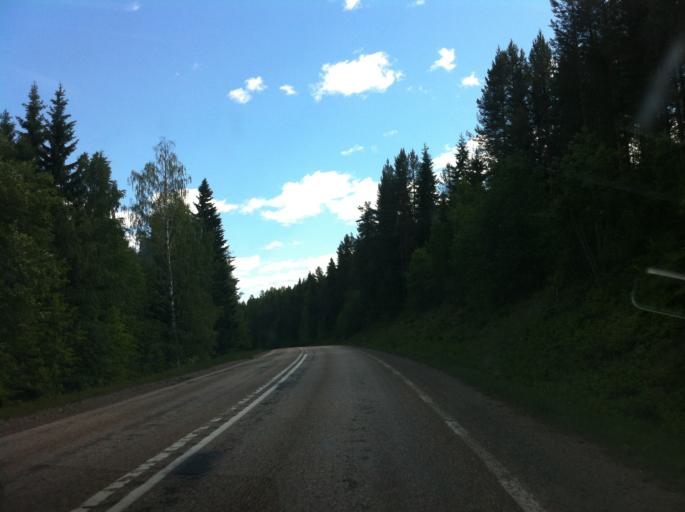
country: SE
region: Gaevleborg
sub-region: Ljusdals Kommun
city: Farila
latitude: 61.9578
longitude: 15.3587
